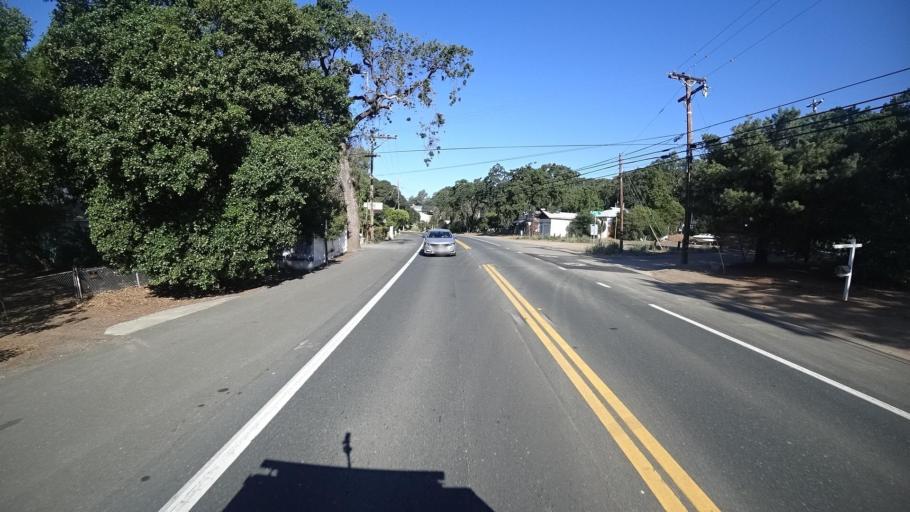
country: US
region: California
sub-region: Lake County
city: Clearlake Oaks
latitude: 39.0216
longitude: -122.7125
